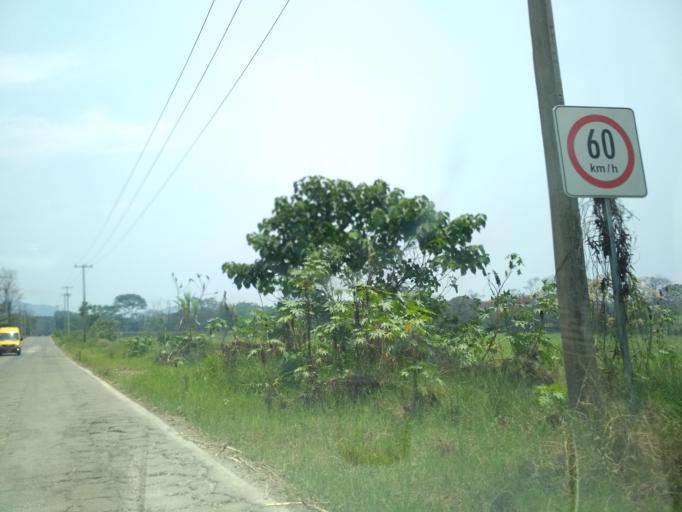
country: MX
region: Veracruz
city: Cosolapa
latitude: 18.5887
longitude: -96.6975
